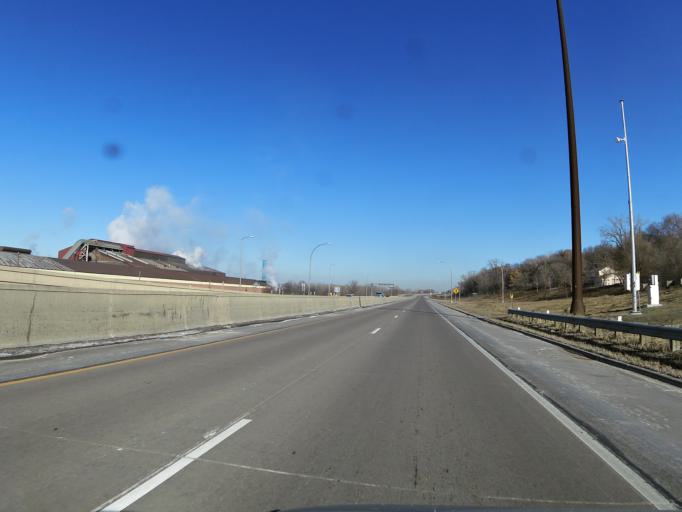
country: US
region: Minnesota
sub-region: Dakota County
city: South Saint Paul
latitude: 44.8935
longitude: -93.0077
